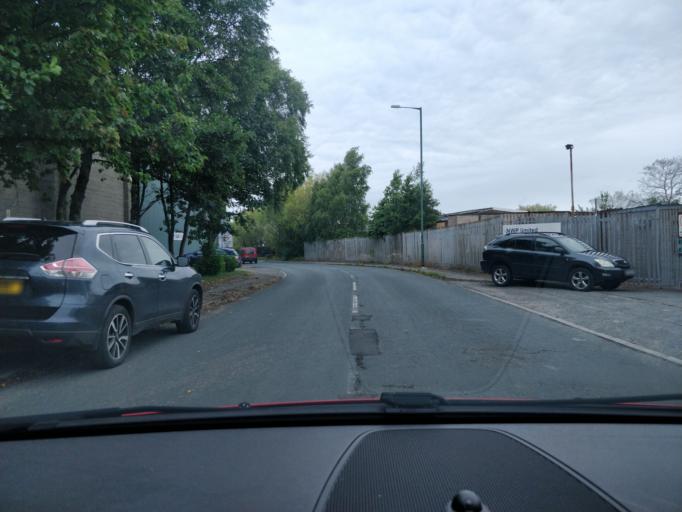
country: GB
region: England
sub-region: Lancashire
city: Ormskirk
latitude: 53.6015
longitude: -2.8656
